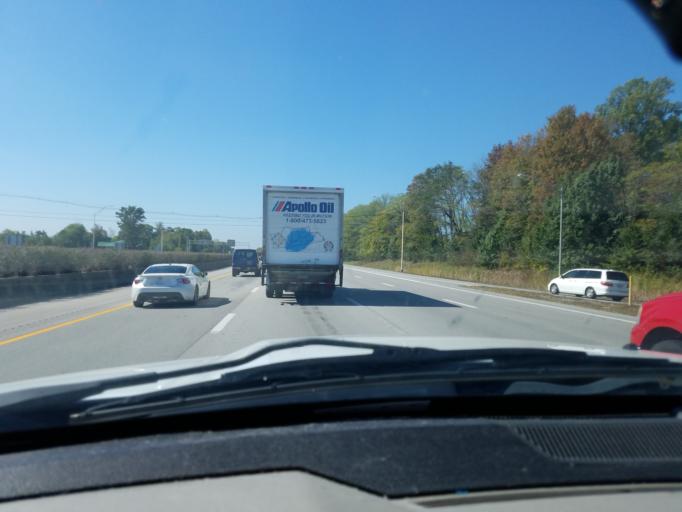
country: US
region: Kentucky
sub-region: Jefferson County
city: Douglass Hills
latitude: 38.2240
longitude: -85.5422
